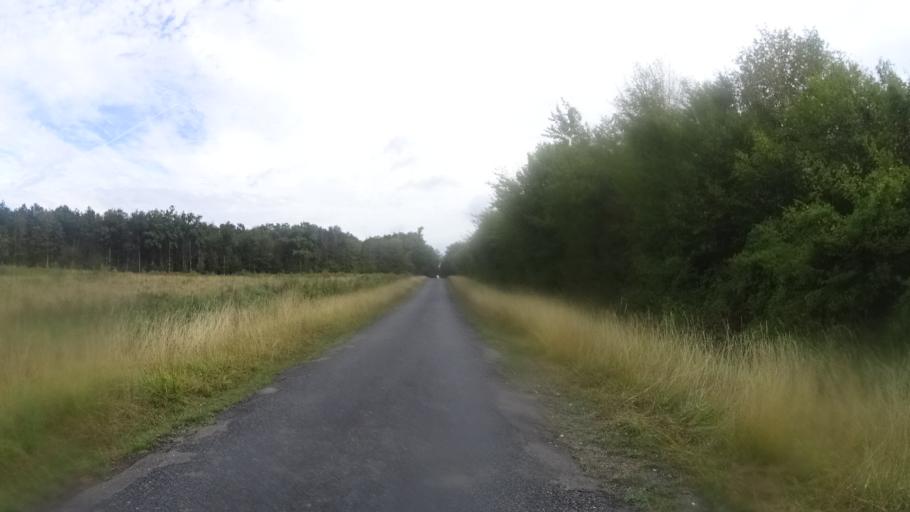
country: FR
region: Centre
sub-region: Departement du Loiret
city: Vitry-aux-Loges
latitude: 48.0091
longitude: 2.2422
